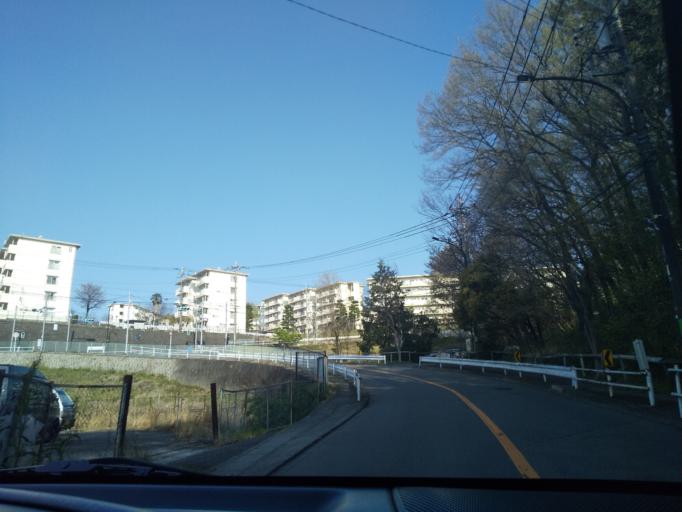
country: JP
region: Tokyo
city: Hino
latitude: 35.6460
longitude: 139.4196
